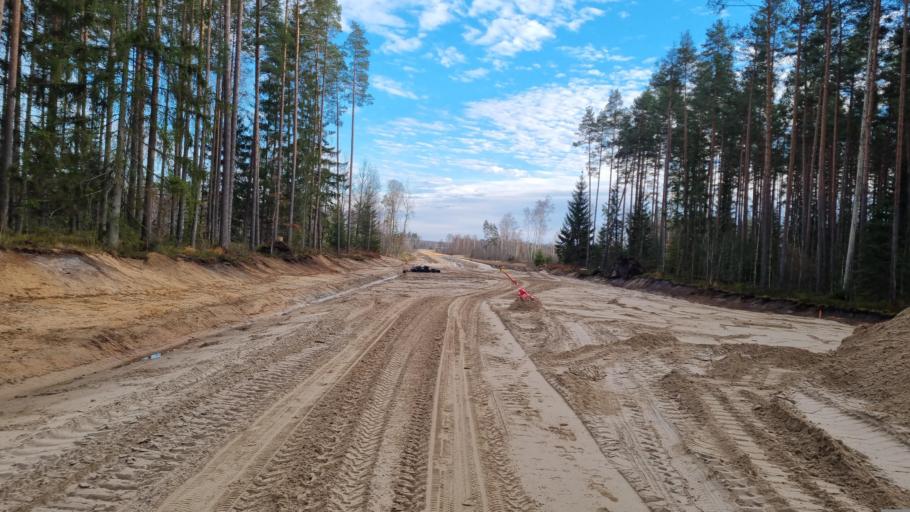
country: LV
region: Kekava
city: Kekava
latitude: 56.7880
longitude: 24.2208
